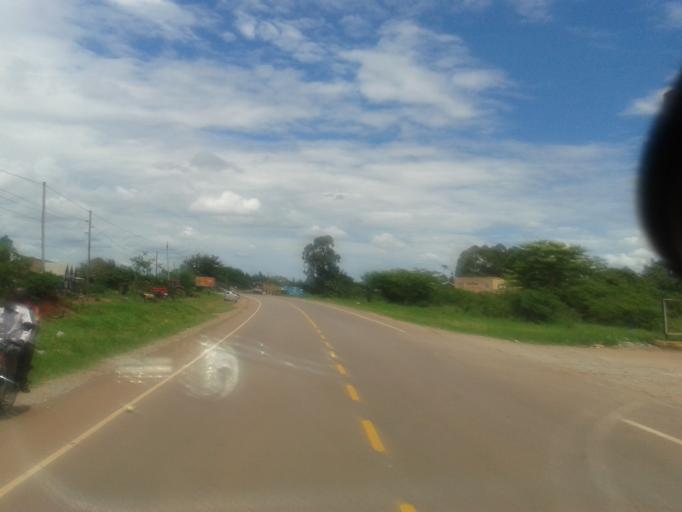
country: UG
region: Western Region
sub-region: Kiryandongo District
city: Kiryandongo
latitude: 1.8032
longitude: 32.0096
